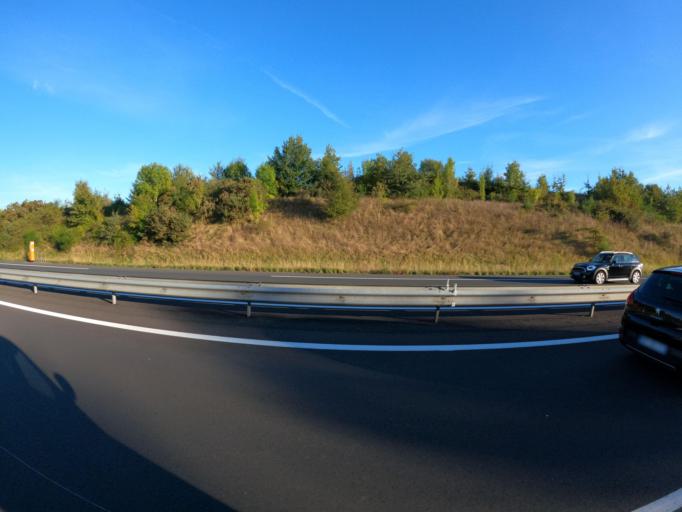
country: FR
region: Pays de la Loire
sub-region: Departement de la Vendee
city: Beaurepaire
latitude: 46.8767
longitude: -1.1135
